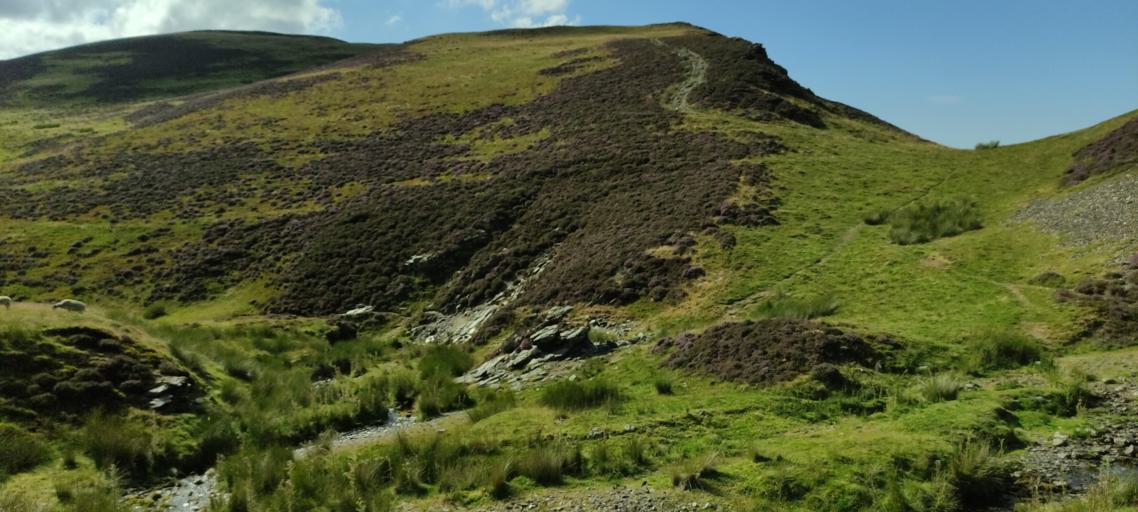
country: GB
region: England
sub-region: Cumbria
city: Keswick
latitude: 54.6903
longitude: -3.1191
